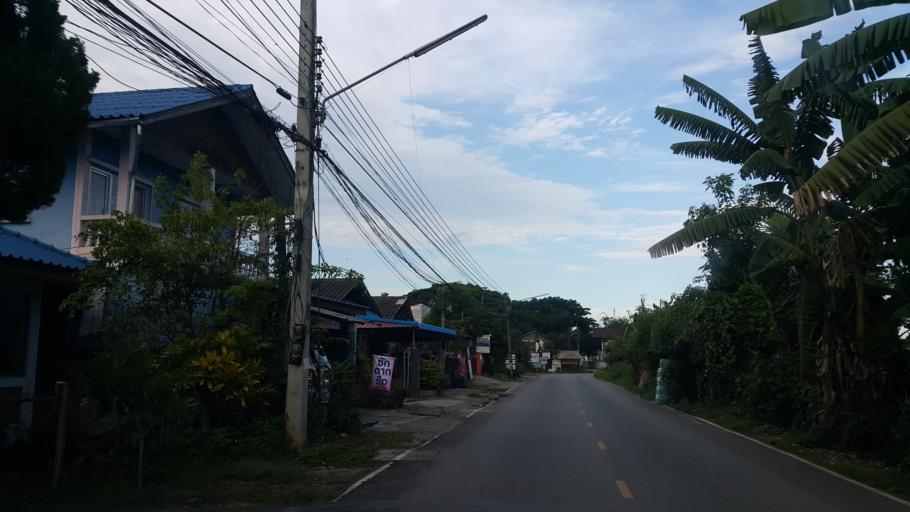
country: TH
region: Chiang Rai
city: Chiang Rai
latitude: 19.9250
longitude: 99.8459
